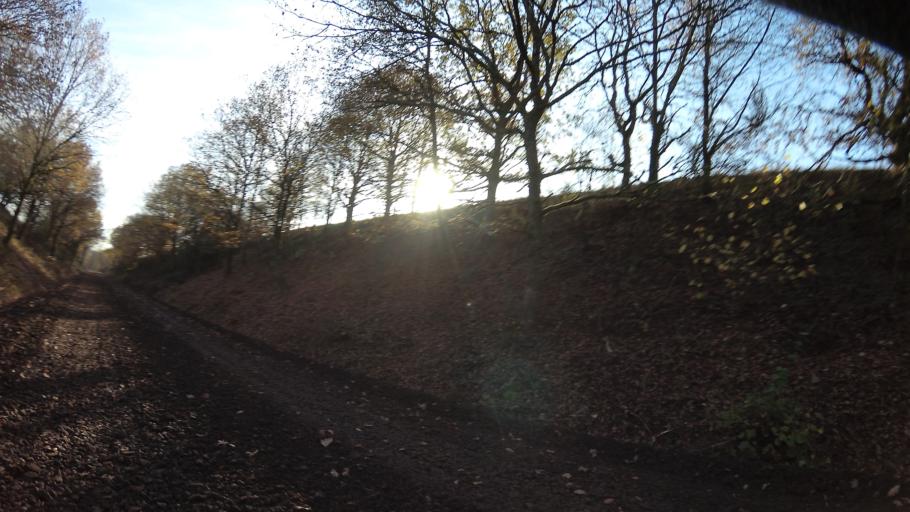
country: DE
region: Rheinland-Pfalz
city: Gimbweiler
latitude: 49.5567
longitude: 7.1753
